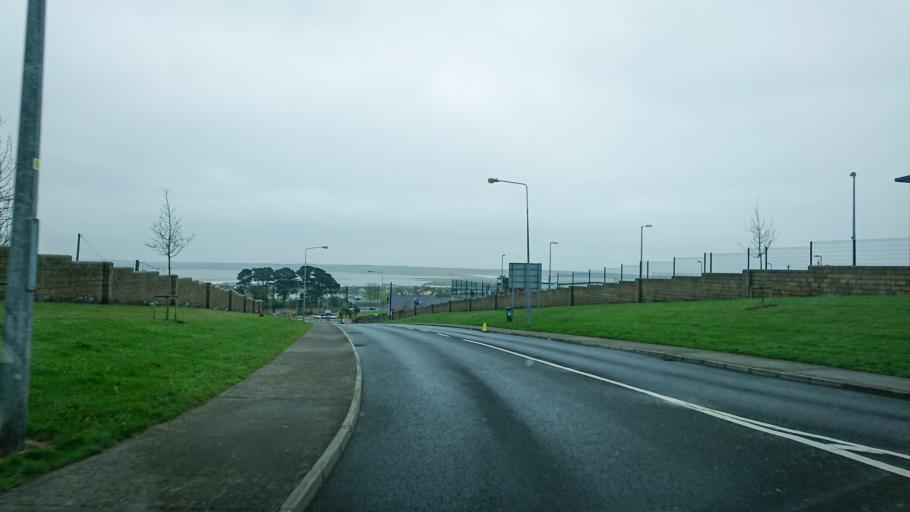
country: IE
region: Munster
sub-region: Waterford
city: Tra Mhor
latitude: 52.1696
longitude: -7.1467
